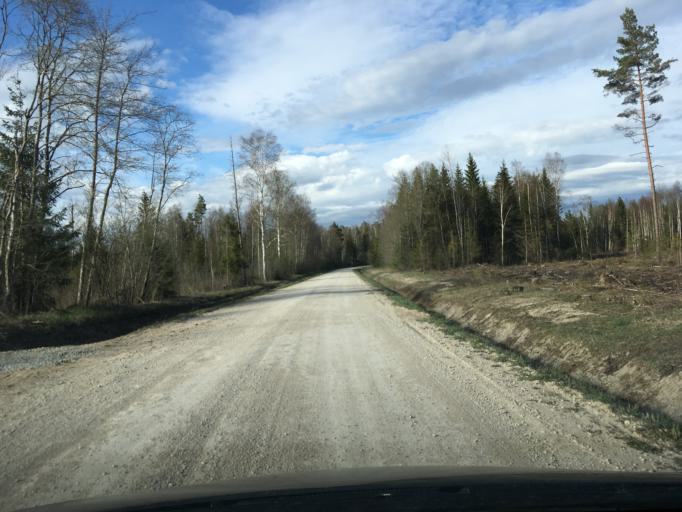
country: EE
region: Raplamaa
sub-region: Maerjamaa vald
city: Marjamaa
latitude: 58.9950
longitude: 24.3682
